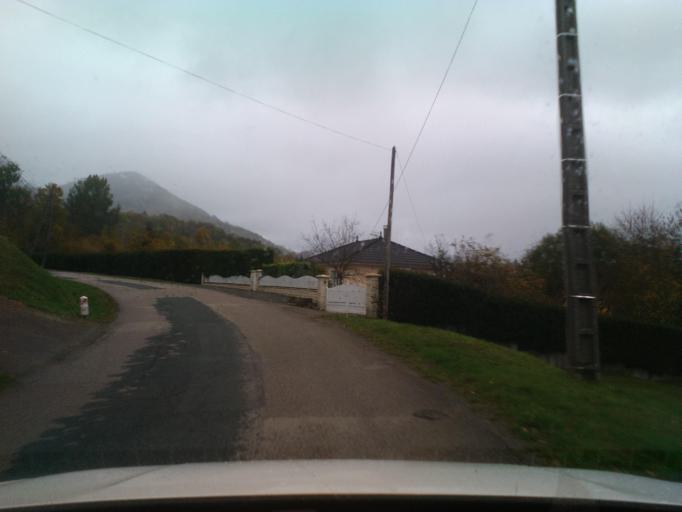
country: FR
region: Lorraine
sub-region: Departement des Vosges
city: Sainte-Marguerite
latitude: 48.2913
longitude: 7.0065
